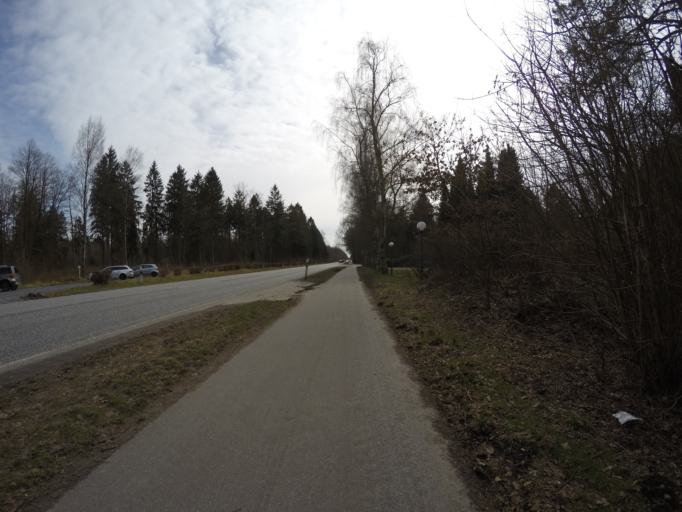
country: DE
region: Schleswig-Holstein
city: Lentfohrden
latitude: 53.8336
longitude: 9.8842
